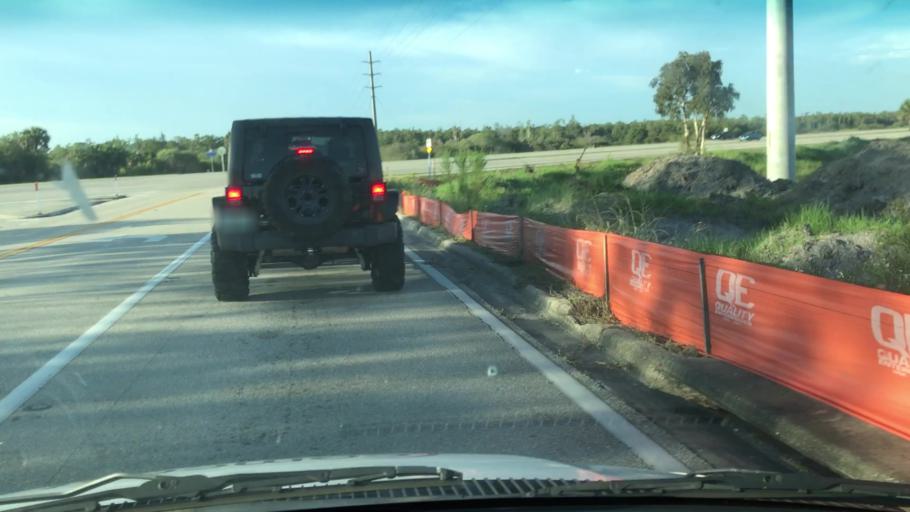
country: US
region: Florida
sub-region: Lee County
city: Villas
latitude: 26.5301
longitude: -81.8469
